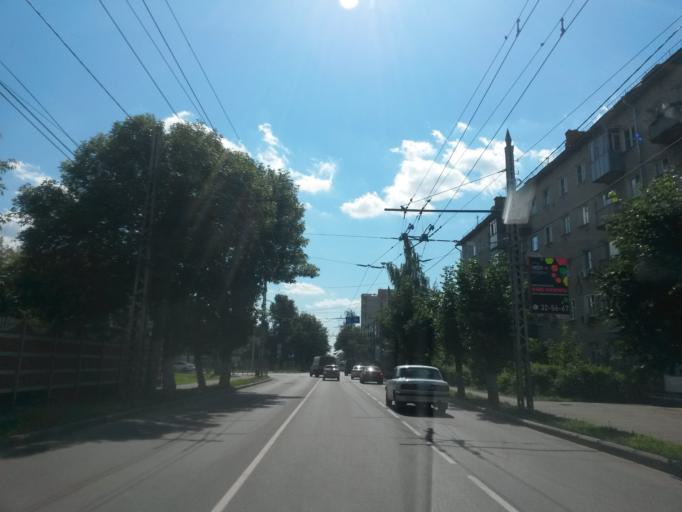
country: RU
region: Ivanovo
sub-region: Gorod Ivanovo
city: Ivanovo
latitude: 56.9885
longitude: 40.9837
